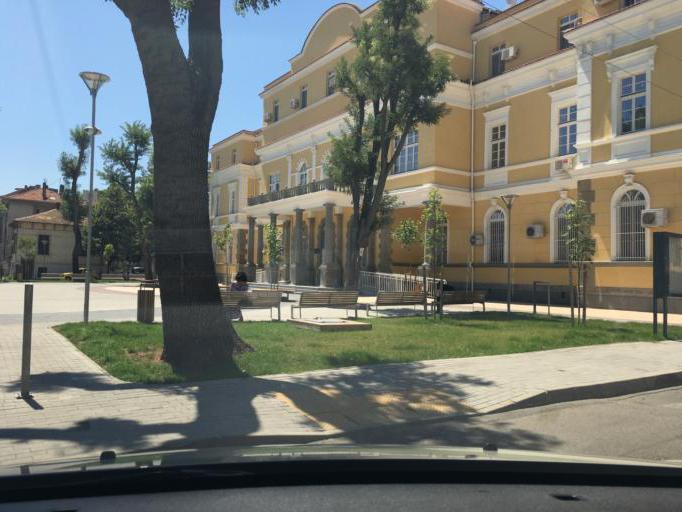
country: BG
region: Burgas
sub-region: Obshtina Burgas
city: Burgas
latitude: 42.4925
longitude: 27.4684
